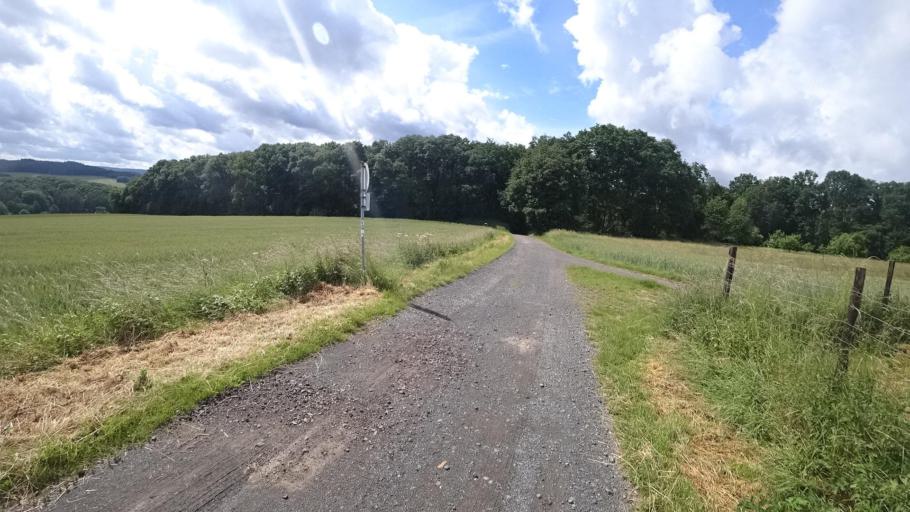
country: DE
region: Rheinland-Pfalz
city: Kalenborn
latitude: 50.5449
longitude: 6.9898
